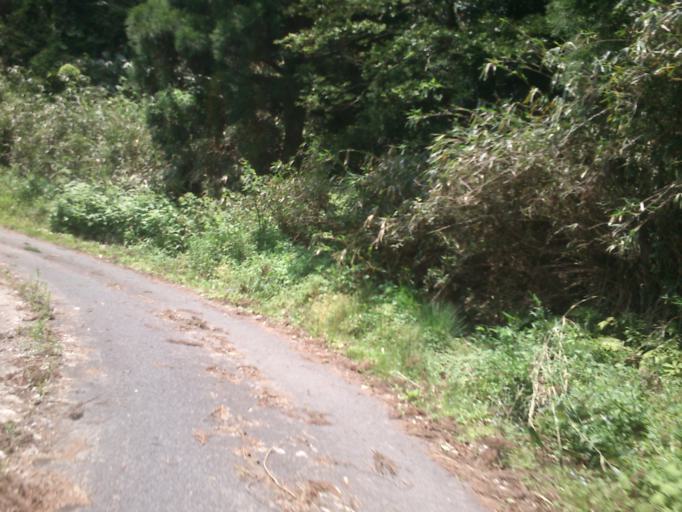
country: JP
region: Kyoto
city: Miyazu
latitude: 35.7001
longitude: 135.1298
